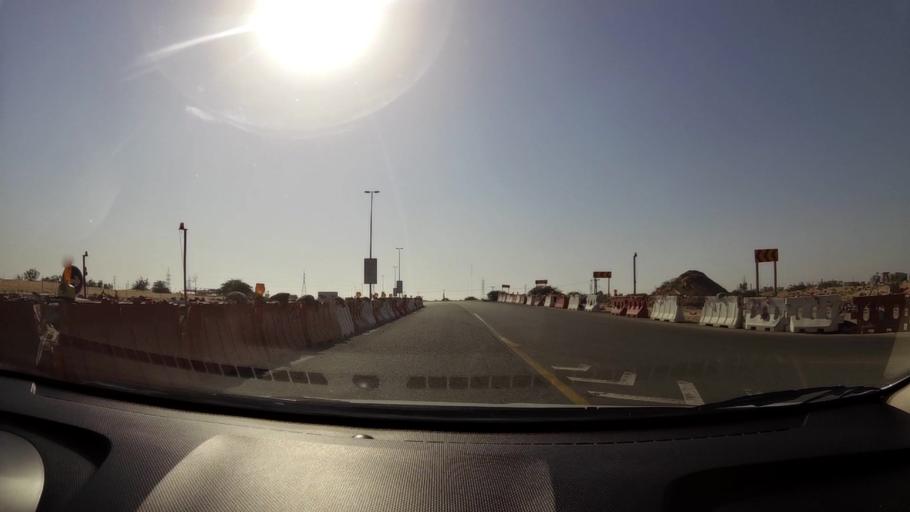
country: AE
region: Umm al Qaywayn
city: Umm al Qaywayn
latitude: 25.4693
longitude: 55.5876
